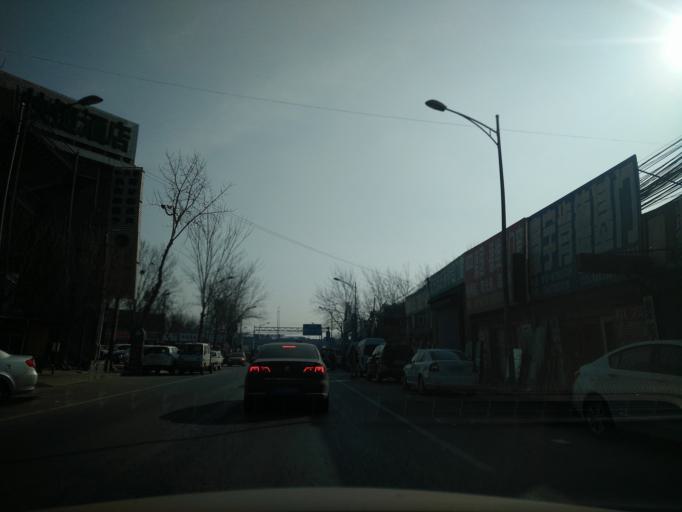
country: CN
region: Beijing
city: Jiugong
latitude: 39.8228
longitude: 116.5044
